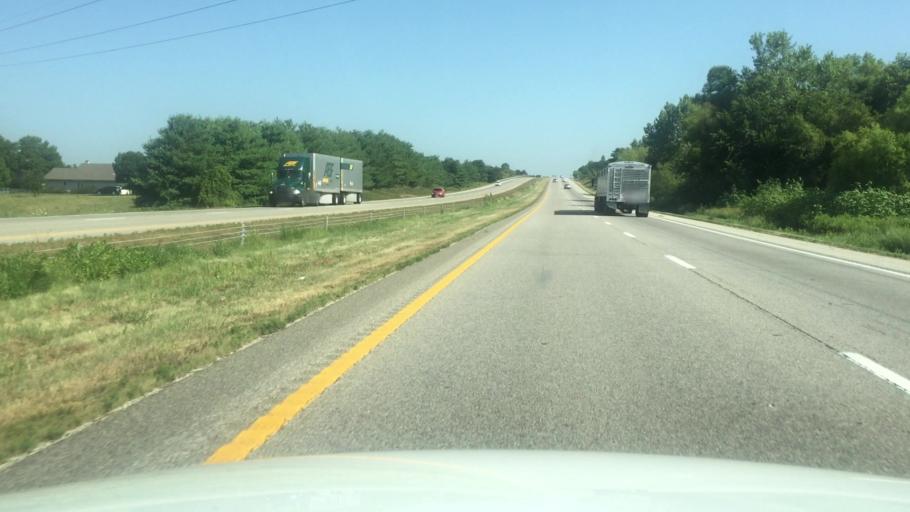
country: US
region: Missouri
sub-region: Clinton County
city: Gower
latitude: 39.5800
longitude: -94.7886
